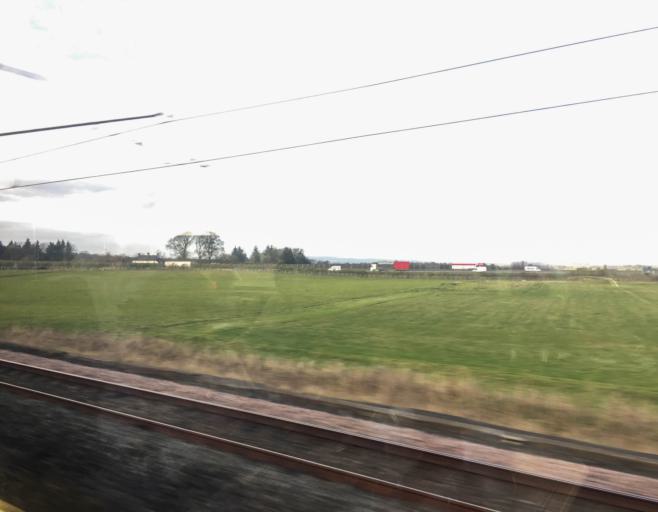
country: GB
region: Scotland
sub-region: Dumfries and Galloway
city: Gretna
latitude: 54.9757
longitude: -3.0181
